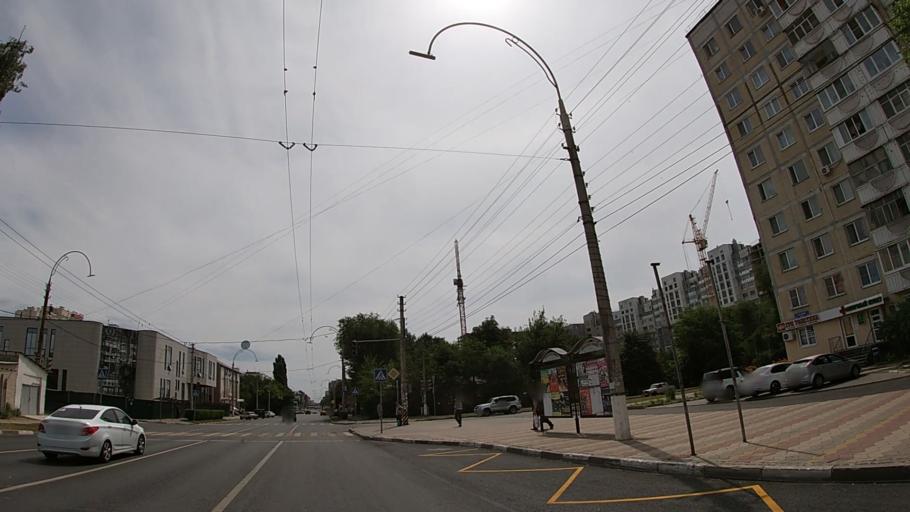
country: RU
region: Belgorod
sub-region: Belgorodskiy Rayon
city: Belgorod
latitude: 50.5997
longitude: 36.5726
